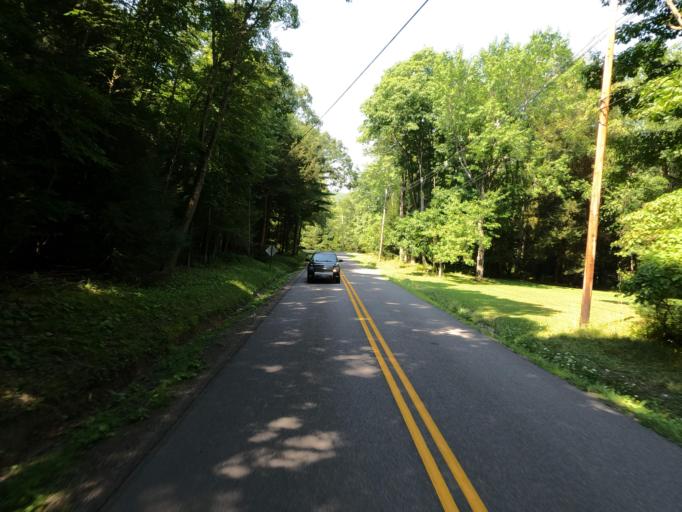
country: US
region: Maryland
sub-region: Garrett County
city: Oakland
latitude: 39.5073
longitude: -79.3889
